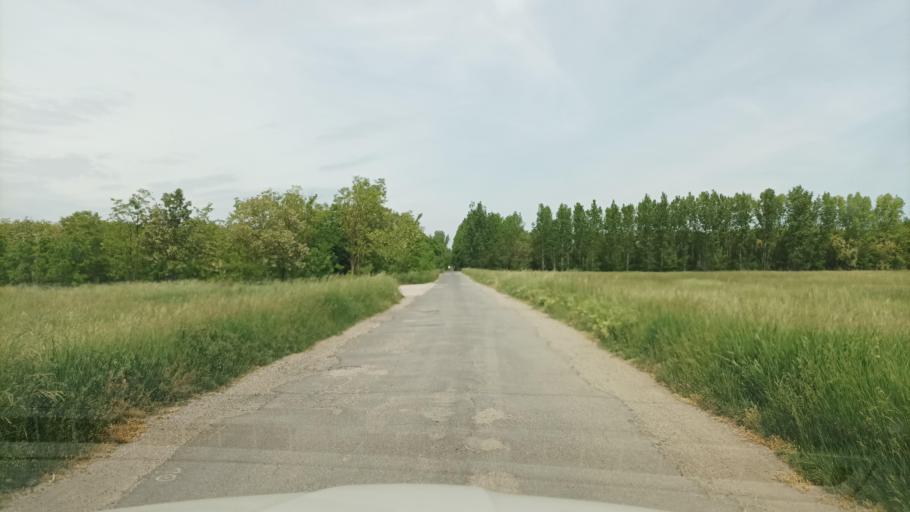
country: HU
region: Fejer
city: Racalmas
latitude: 47.0768
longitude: 18.9425
